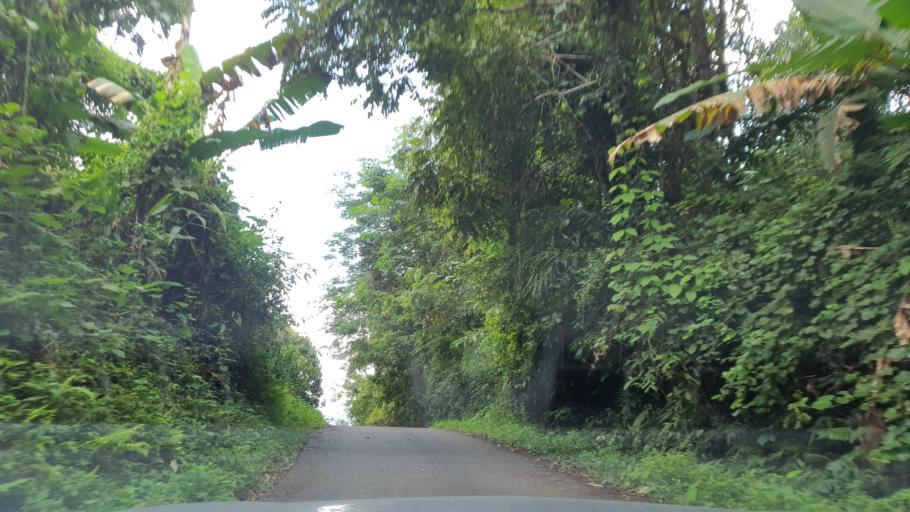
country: TH
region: Chiang Mai
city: Mae On
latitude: 18.9324
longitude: 99.3117
